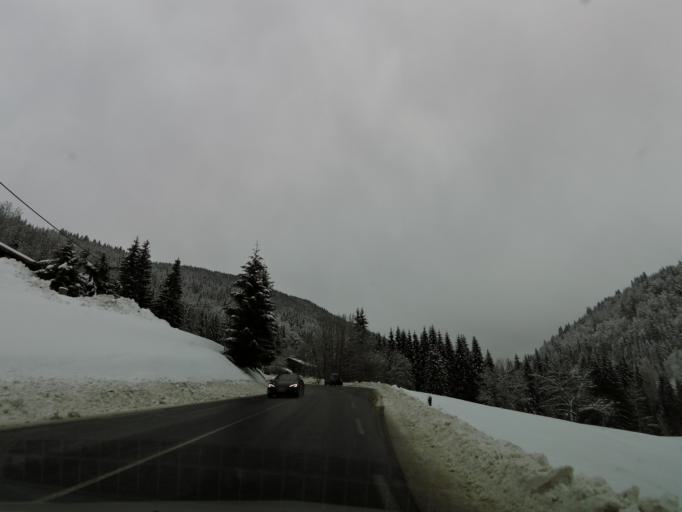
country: FR
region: Rhone-Alpes
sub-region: Departement de la Haute-Savoie
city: Morzine
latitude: 46.1809
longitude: 6.6829
